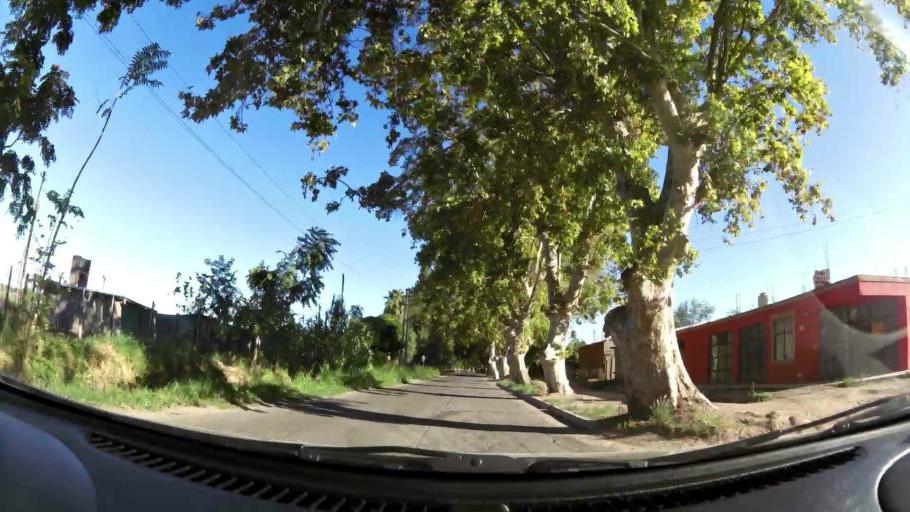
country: AR
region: Mendoza
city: Las Heras
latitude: -32.8487
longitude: -68.8273
